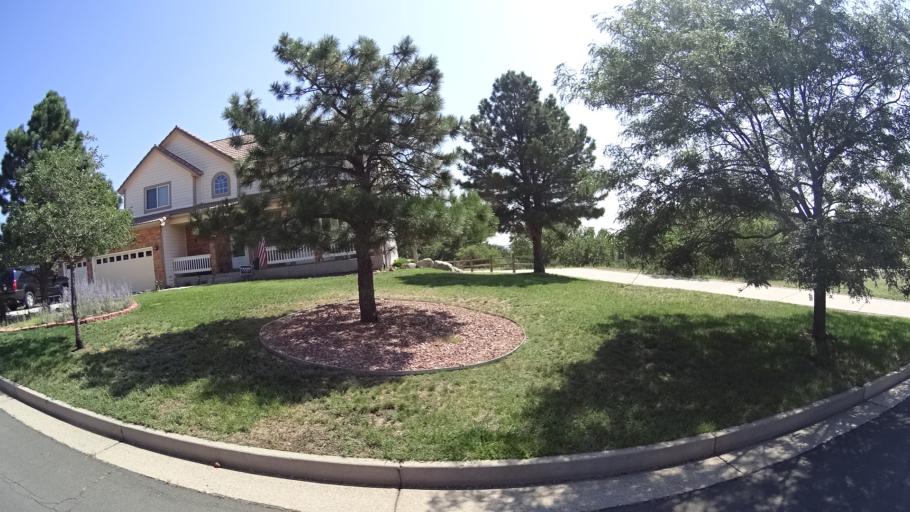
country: US
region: Colorado
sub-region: El Paso County
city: Manitou Springs
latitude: 38.9189
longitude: -104.8742
